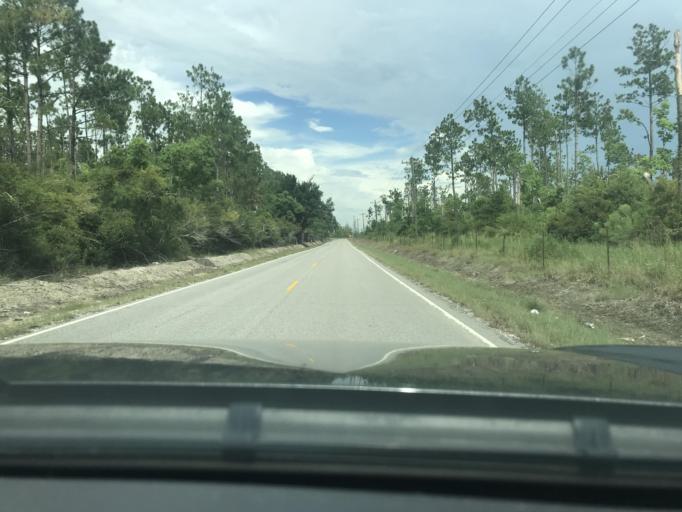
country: US
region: Louisiana
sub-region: Calcasieu Parish
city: Moss Bluff
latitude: 30.3885
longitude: -93.2368
